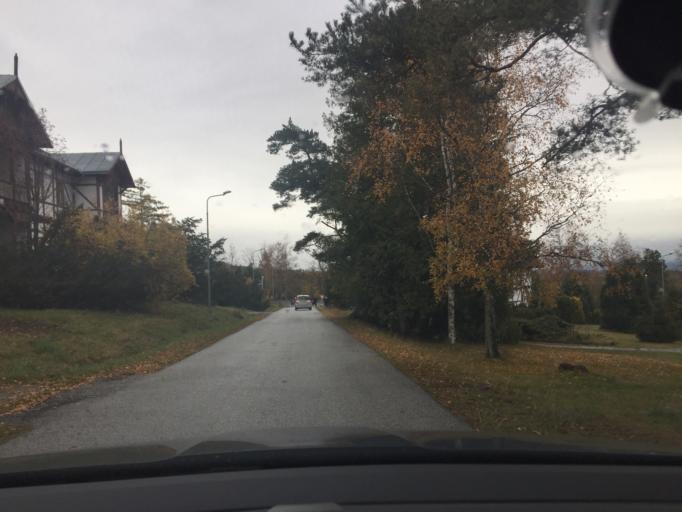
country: SK
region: Presovsky
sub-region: Okres Poprad
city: Vysoke Tatry
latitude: 49.1324
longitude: 20.2400
